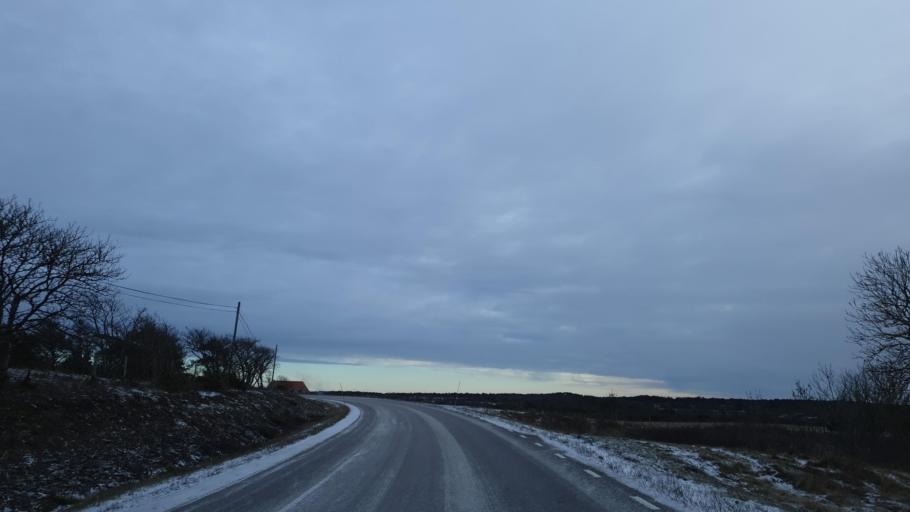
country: SE
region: Gotland
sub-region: Gotland
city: Slite
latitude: 57.4202
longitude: 18.8903
